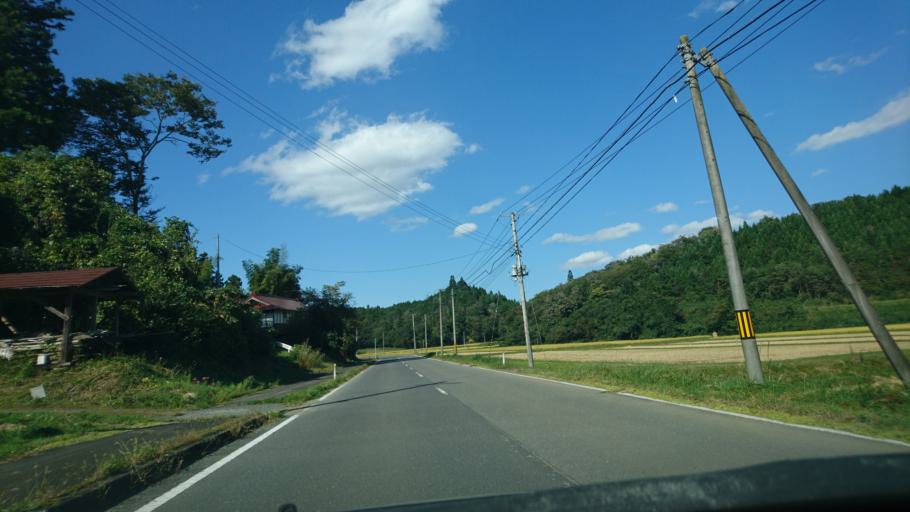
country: JP
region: Iwate
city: Ichinoseki
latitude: 38.8641
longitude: 141.0452
